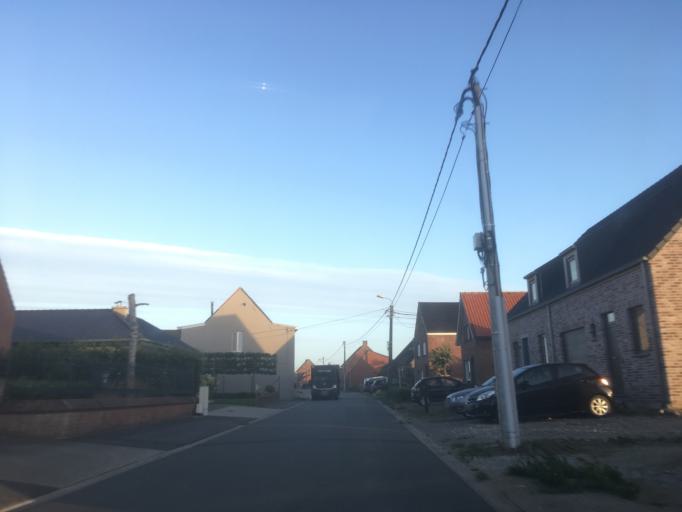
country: BE
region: Flanders
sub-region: Provincie West-Vlaanderen
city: Hooglede
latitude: 51.0213
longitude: 3.0942
